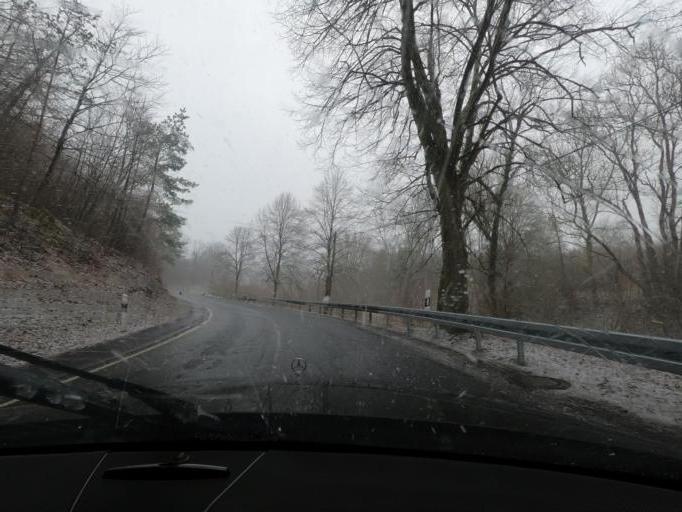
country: DE
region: Thuringia
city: Effelder
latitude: 51.2456
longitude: 10.2457
